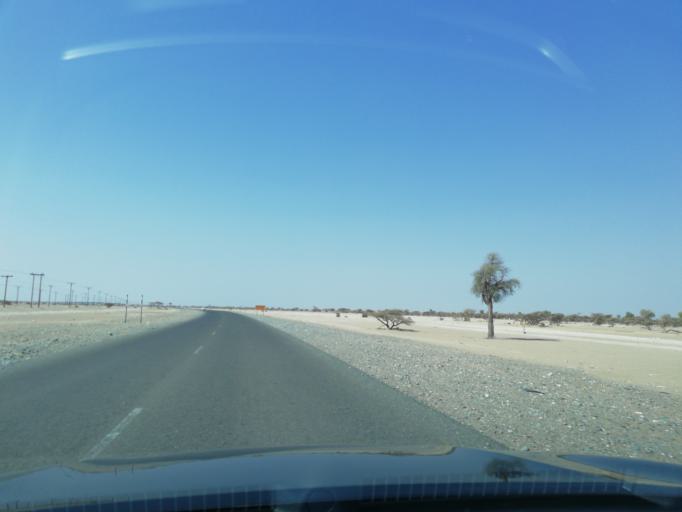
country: OM
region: Muhafazat ad Dakhiliyah
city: Adam
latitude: 22.3391
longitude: 58.0679
